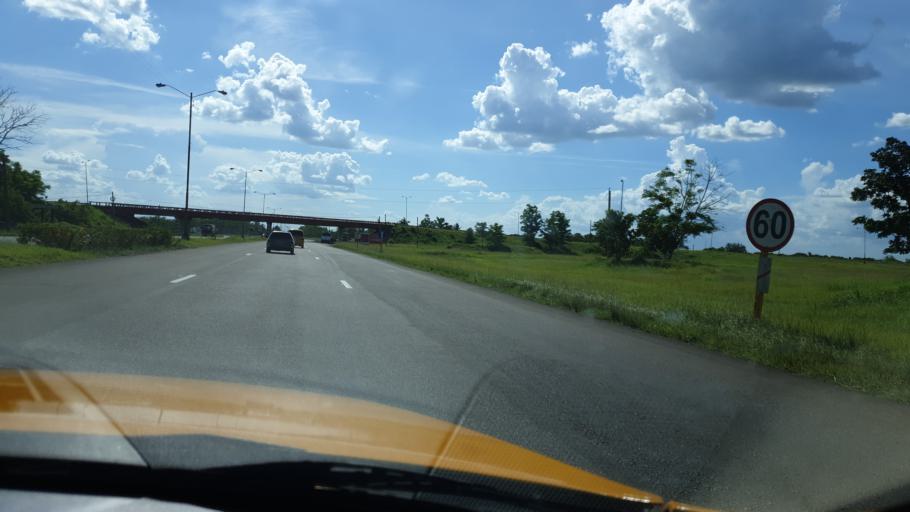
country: CU
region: Cienfuegos
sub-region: Municipio de Aguada de Pasajeros
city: Aguada de Pasajeros
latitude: 22.4034
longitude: -80.8610
